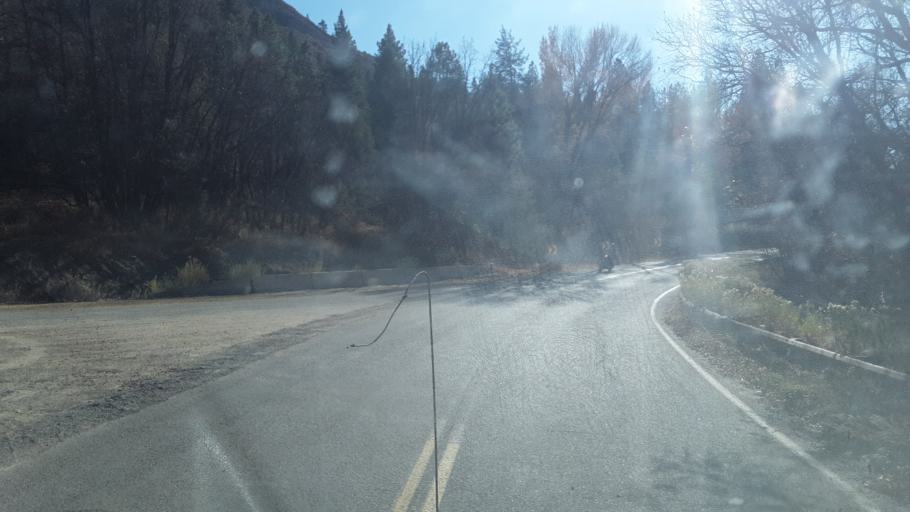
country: US
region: Colorado
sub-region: La Plata County
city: Durango
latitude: 37.4197
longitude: -107.8006
